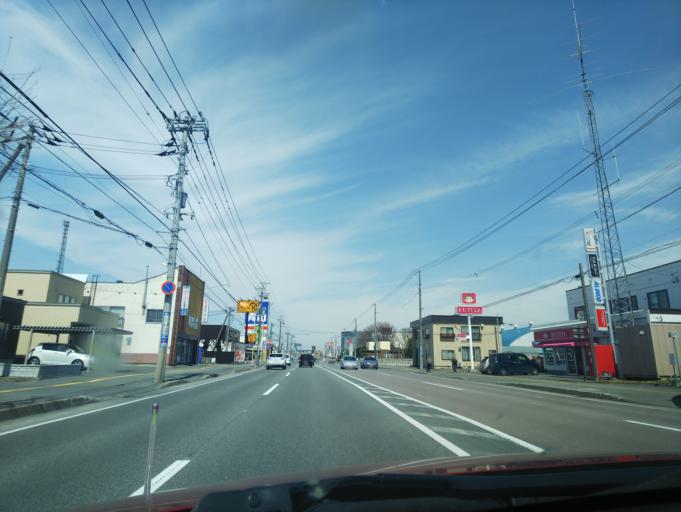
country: JP
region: Hokkaido
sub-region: Asahikawa-shi
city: Asahikawa
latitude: 43.7768
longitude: 142.3846
